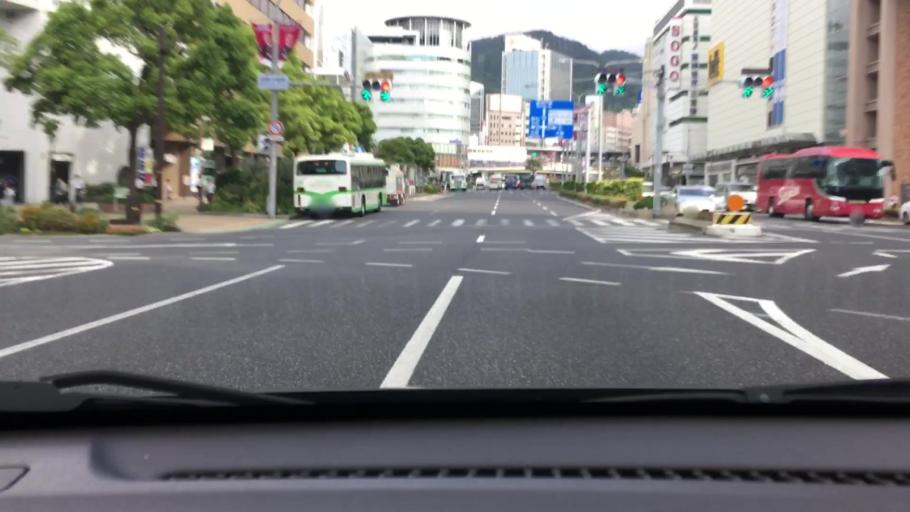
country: JP
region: Hyogo
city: Kobe
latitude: 34.6914
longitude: 135.1954
